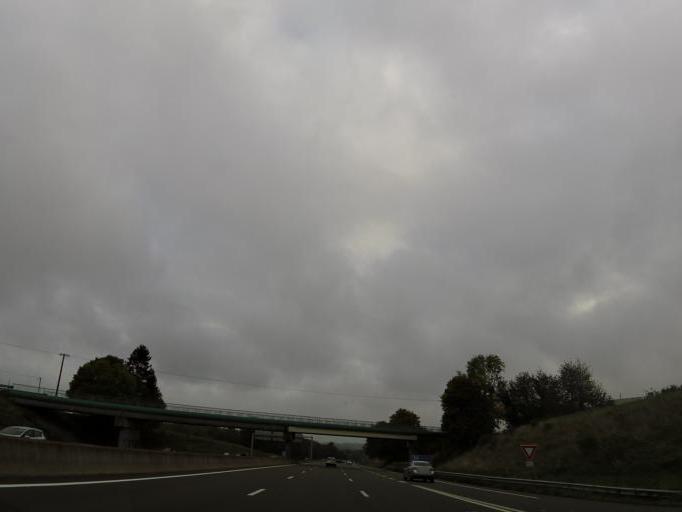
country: FR
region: Ile-de-France
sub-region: Departement de Seine-et-Marne
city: Saint-Germain-sur-Morin
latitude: 48.8626
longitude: 2.8467
